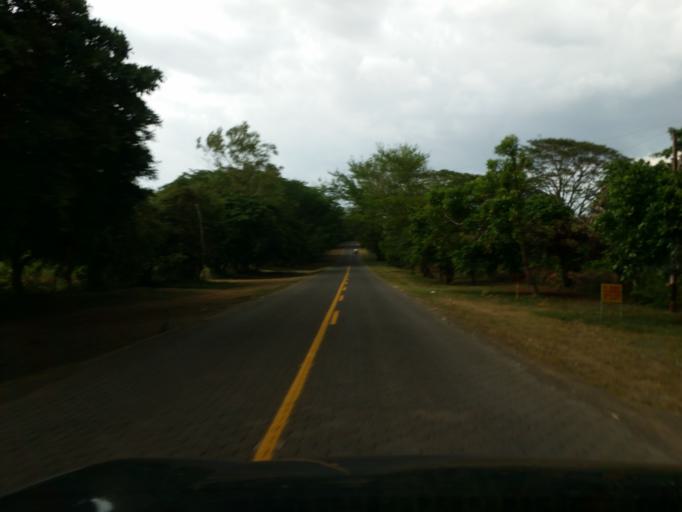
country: NI
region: Managua
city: Carlos Fonseca Amador
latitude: 11.9965
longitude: -86.5162
